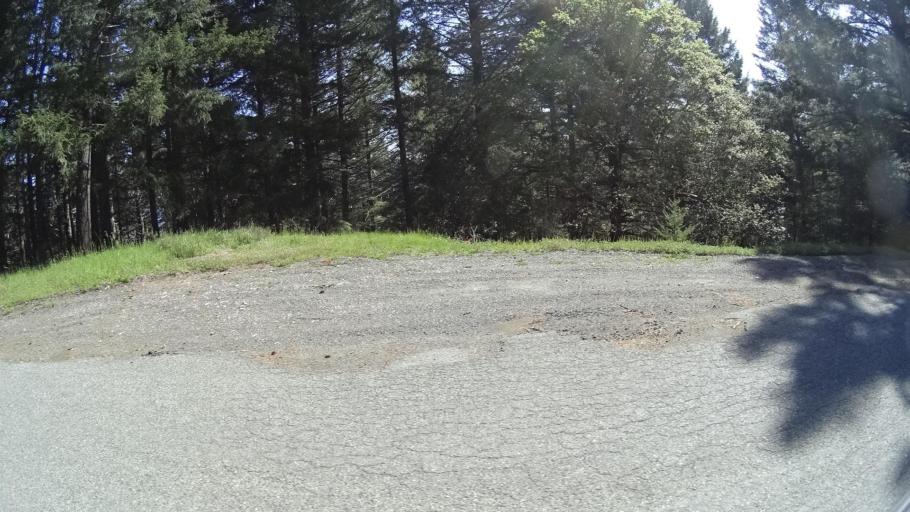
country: US
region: California
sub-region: Humboldt County
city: Redway
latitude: 40.0716
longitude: -123.6496
